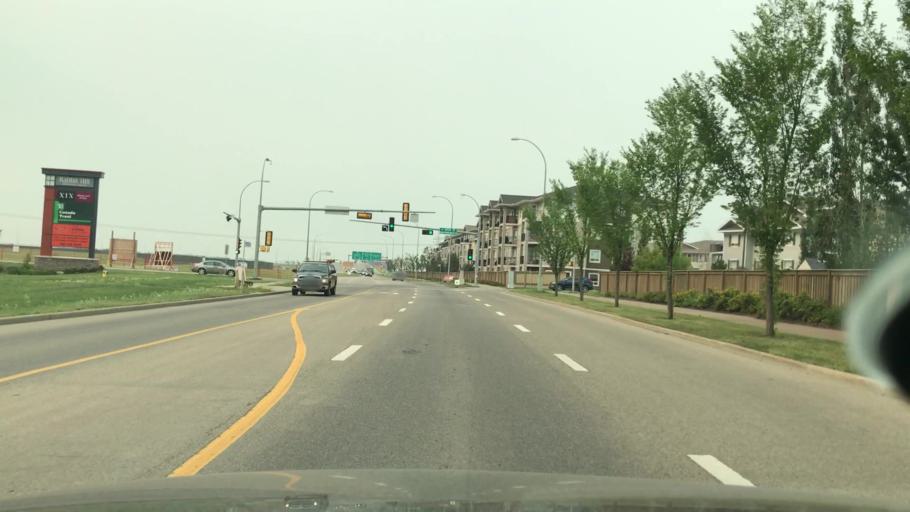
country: CA
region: Alberta
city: Edmonton
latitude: 53.4355
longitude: -113.5740
